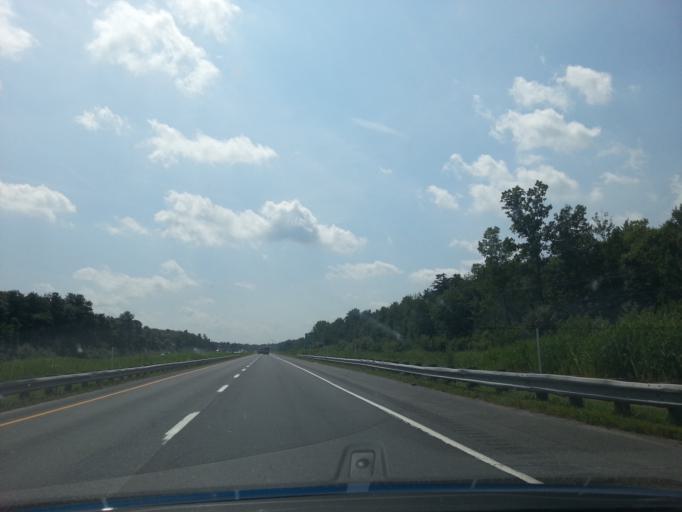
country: CA
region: Quebec
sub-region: Centre-du-Quebec
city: Drummondville
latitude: 45.9215
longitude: -72.4745
